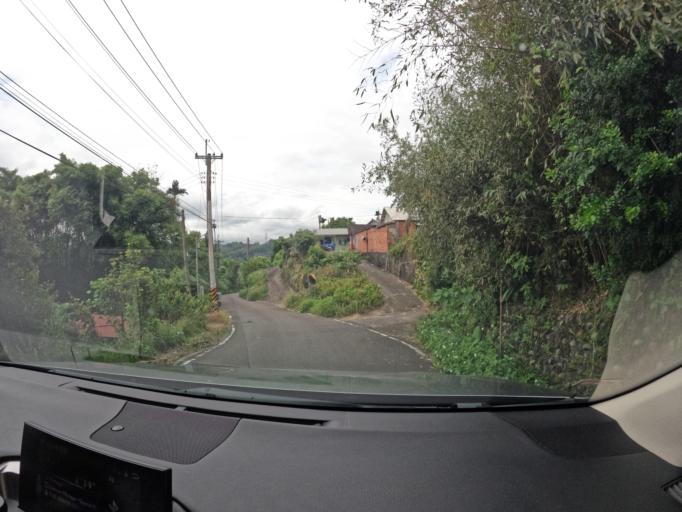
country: TW
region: Taiwan
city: Fengyuan
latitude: 24.3468
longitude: 120.8736
